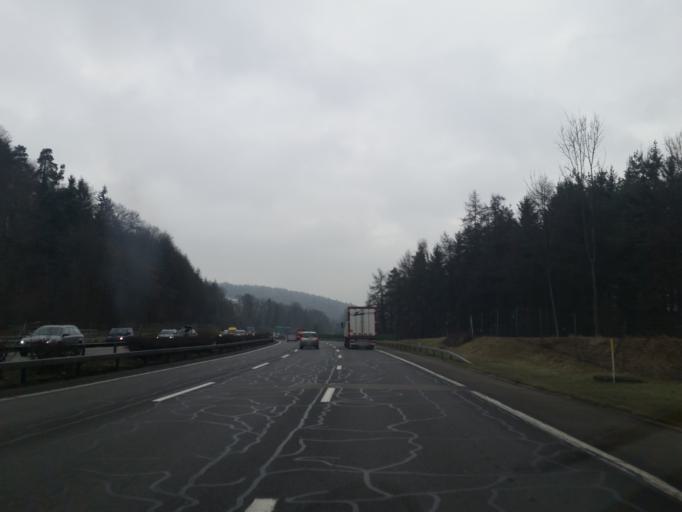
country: CH
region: Zurich
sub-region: Bezirk Winterthur
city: Toss
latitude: 47.4674
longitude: 8.7074
